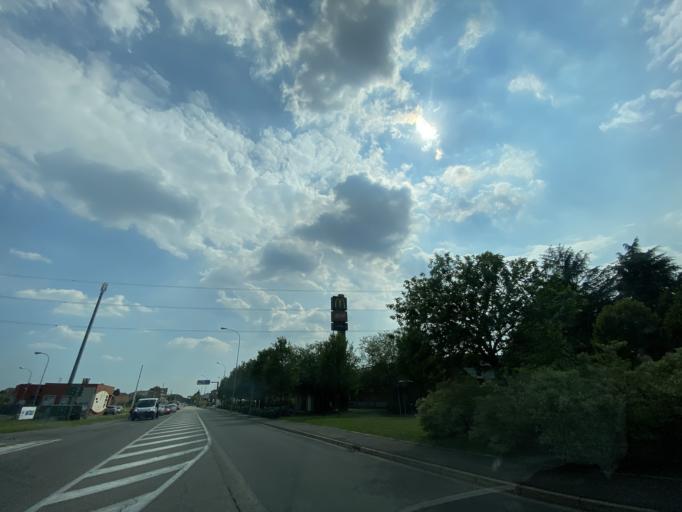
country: IT
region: Lombardy
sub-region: Provincia di Monza e Brianza
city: Nova Milanese
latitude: 45.6012
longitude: 9.2008
